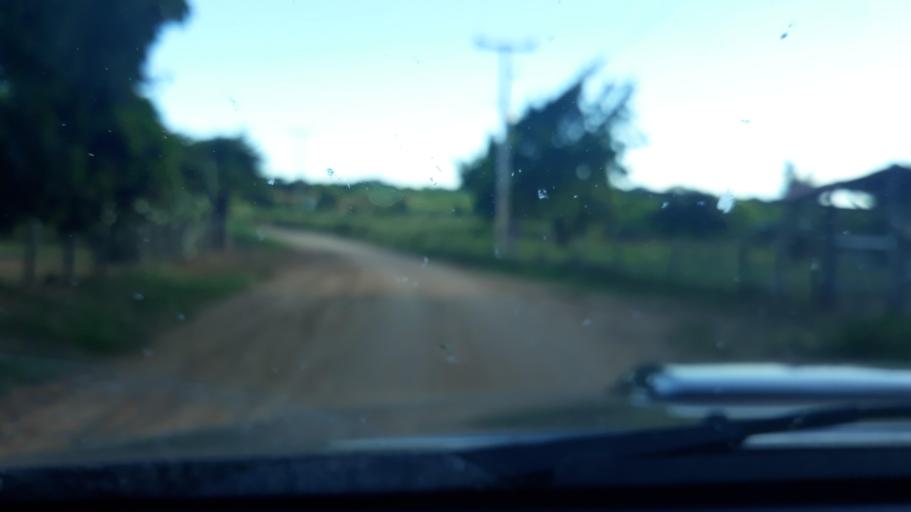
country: BR
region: Bahia
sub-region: Riacho De Santana
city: Riacho de Santana
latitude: -13.8312
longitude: -42.7303
